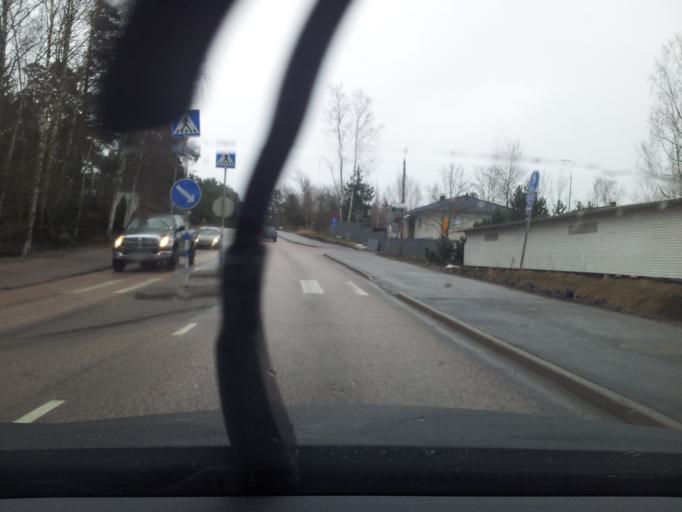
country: FI
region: Uusimaa
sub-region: Helsinki
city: Espoo
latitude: 60.1766
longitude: 24.6862
